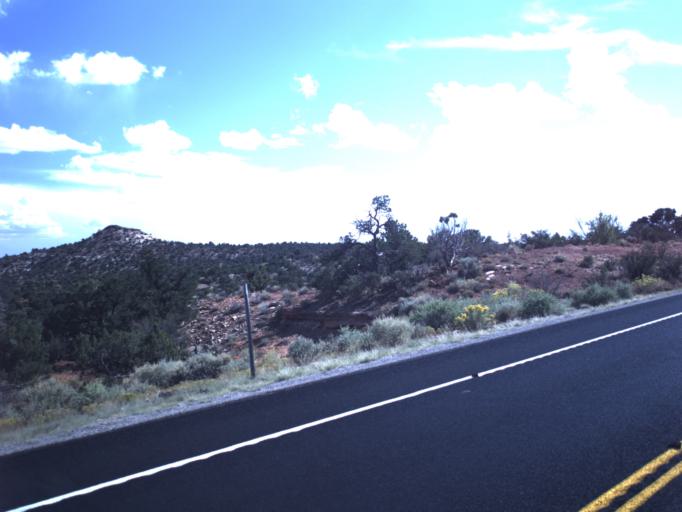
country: US
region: Utah
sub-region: Grand County
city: Moab
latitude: 38.5644
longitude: -109.7932
